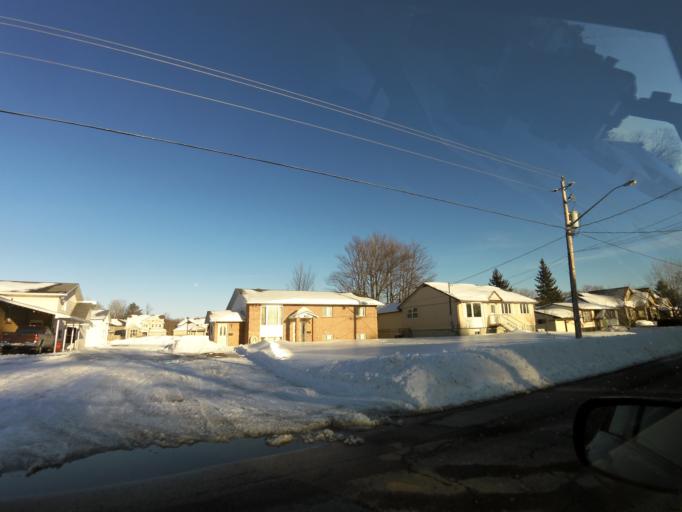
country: CA
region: Ontario
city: Ottawa
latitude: 45.4335
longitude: -75.5194
